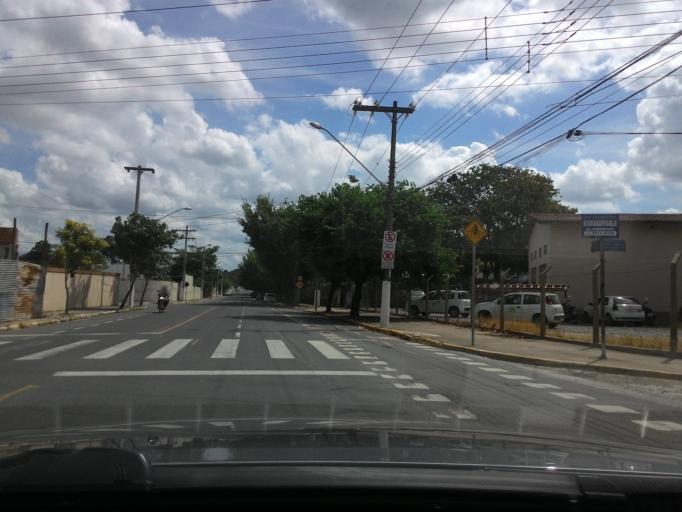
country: BR
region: Sao Paulo
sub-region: Registro
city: Registro
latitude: -24.5030
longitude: -47.8556
